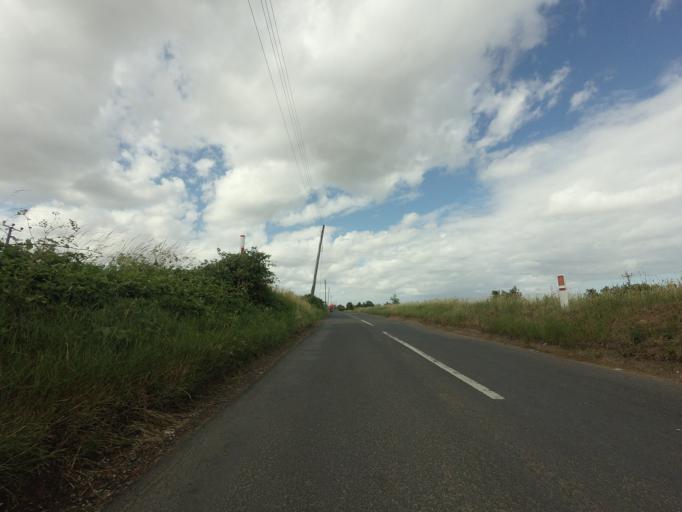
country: GB
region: England
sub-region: Medway
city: Allhallows
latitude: 51.4575
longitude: 0.6372
